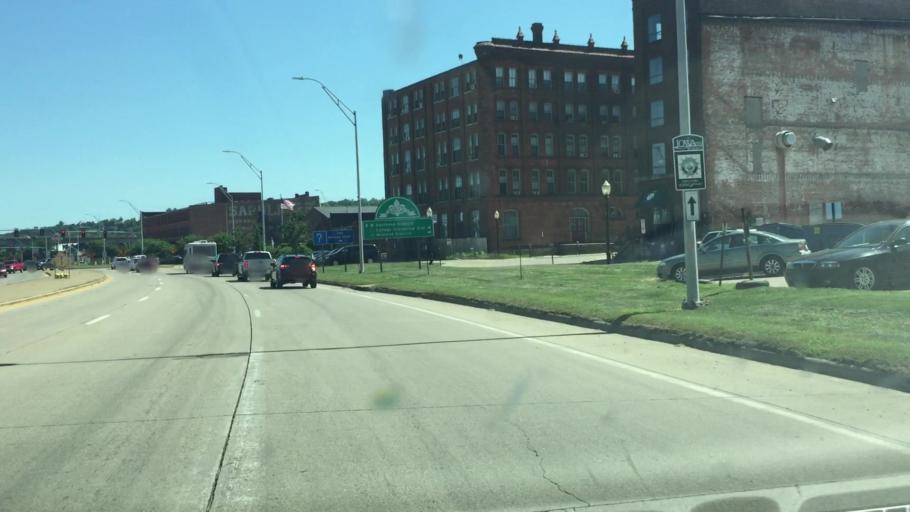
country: US
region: Iowa
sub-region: Dubuque County
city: Dubuque
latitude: 42.4958
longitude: -90.6633
